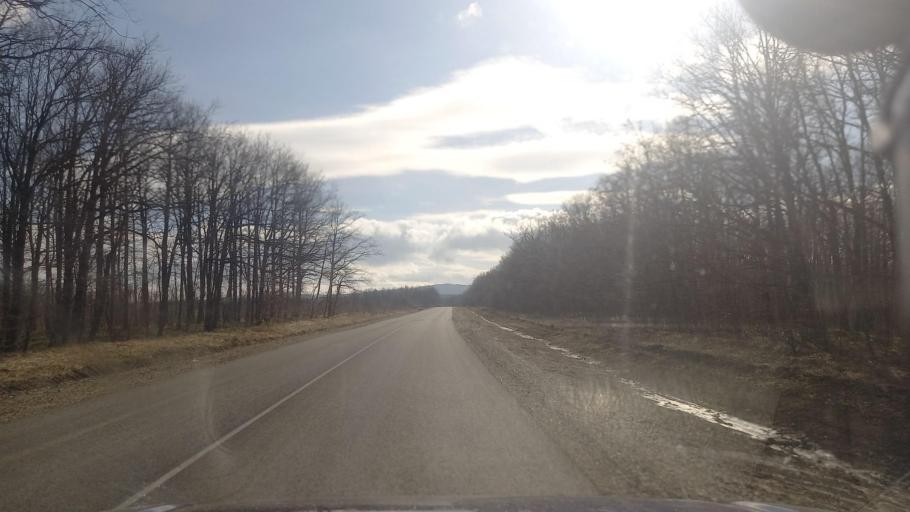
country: RU
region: Krasnodarskiy
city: Novodmitriyevskaya
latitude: 44.7356
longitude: 38.9956
